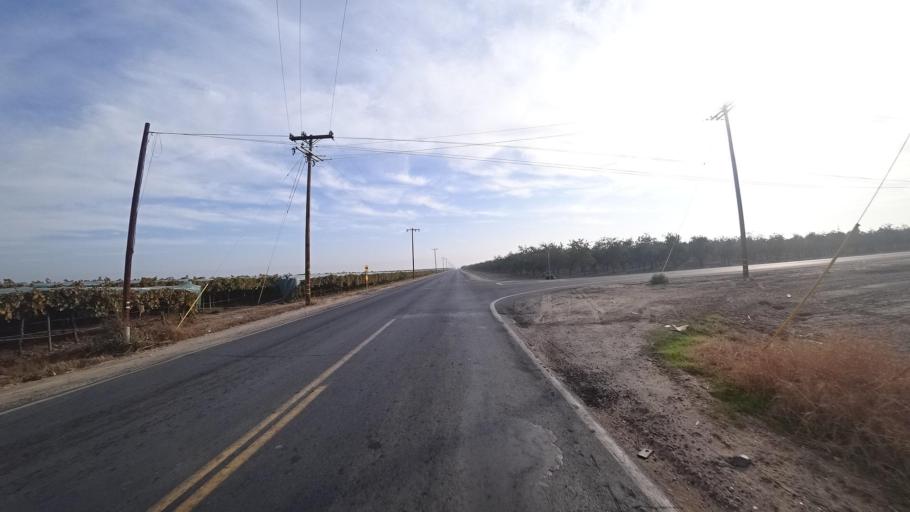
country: US
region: California
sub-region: Kern County
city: Delano
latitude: 35.7905
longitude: -119.2145
